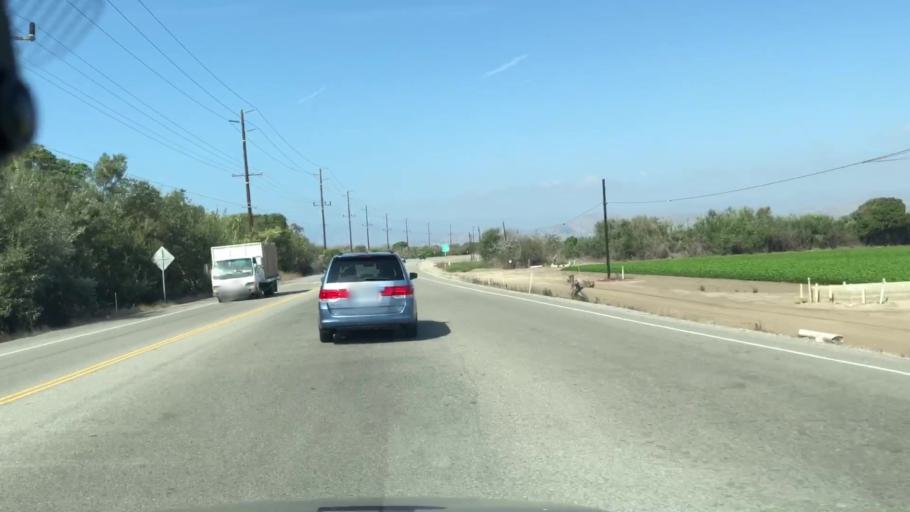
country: US
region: California
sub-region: Ventura County
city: Oxnard Shores
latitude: 34.2197
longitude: -119.2544
